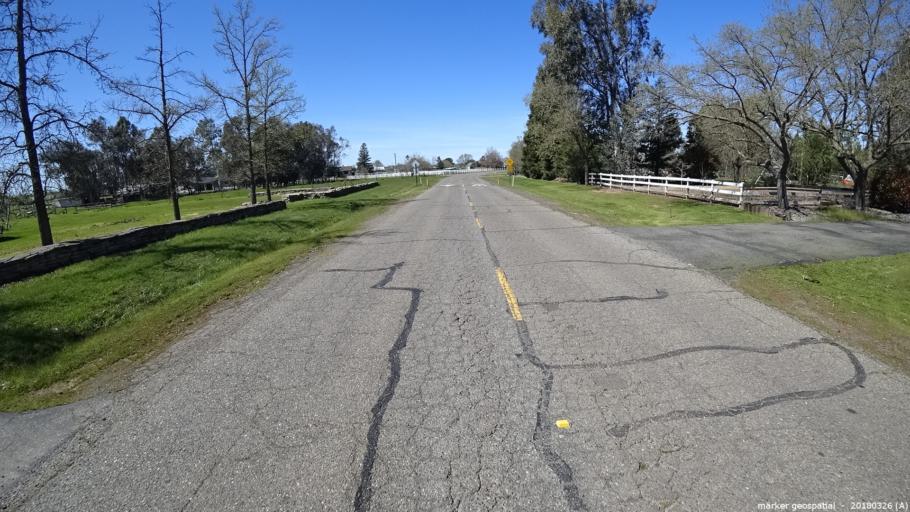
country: US
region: California
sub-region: Sacramento County
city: Wilton
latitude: 38.4813
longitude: -121.2381
